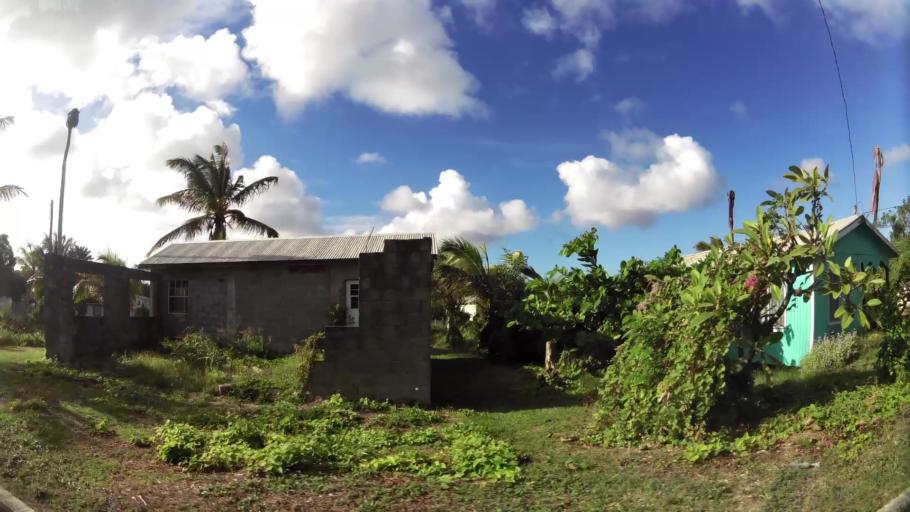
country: AG
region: Saint Peter
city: All Saints
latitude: 17.0676
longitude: -61.7928
